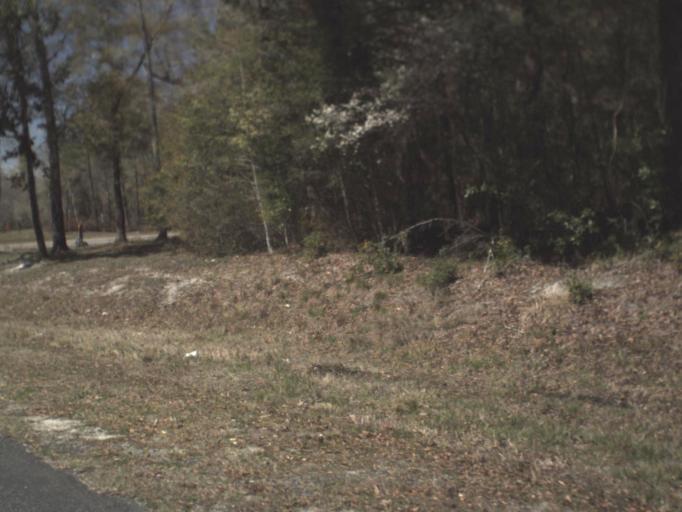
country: US
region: Florida
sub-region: Wakulla County
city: Crawfordville
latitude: 30.2436
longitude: -84.3120
